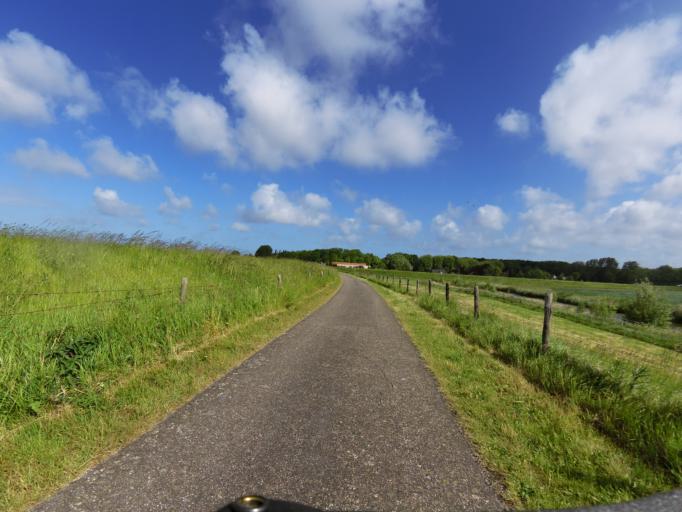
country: NL
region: Zeeland
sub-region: Schouwen-Duiveland
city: Scharendijke
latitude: 51.6704
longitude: 3.9430
